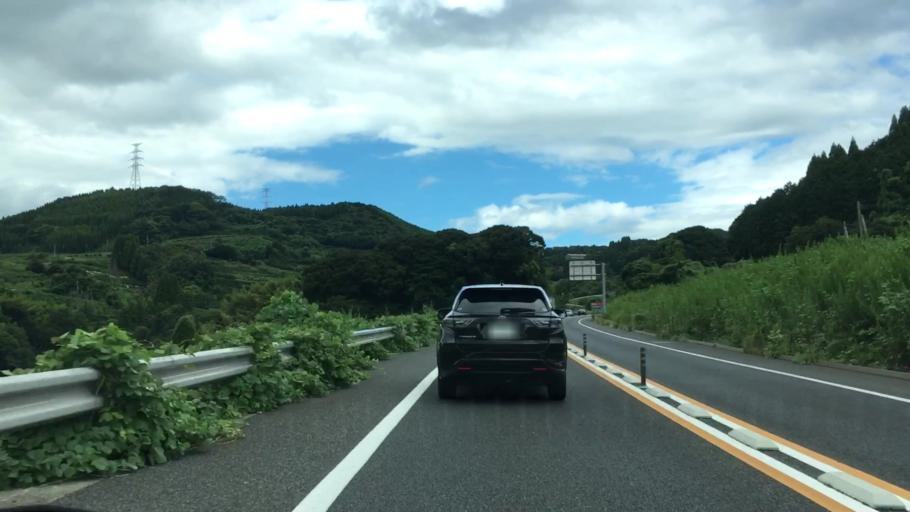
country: JP
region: Saga Prefecture
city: Karatsu
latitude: 33.3938
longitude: 129.9349
